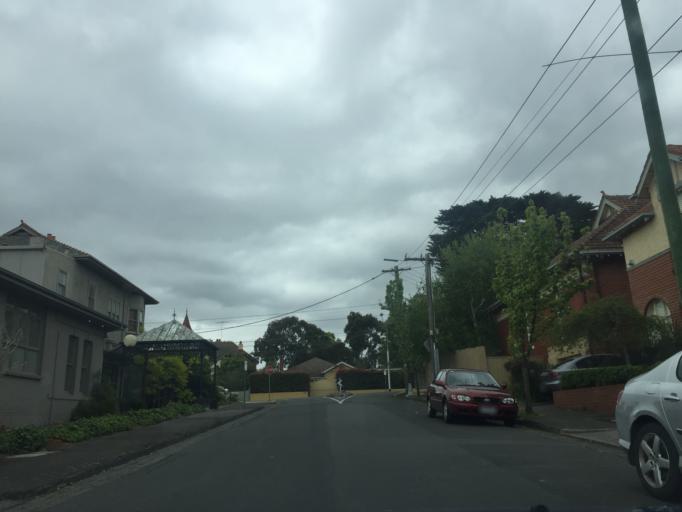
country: AU
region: Victoria
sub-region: Boroondara
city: Kew East
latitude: -37.8092
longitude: 145.0468
